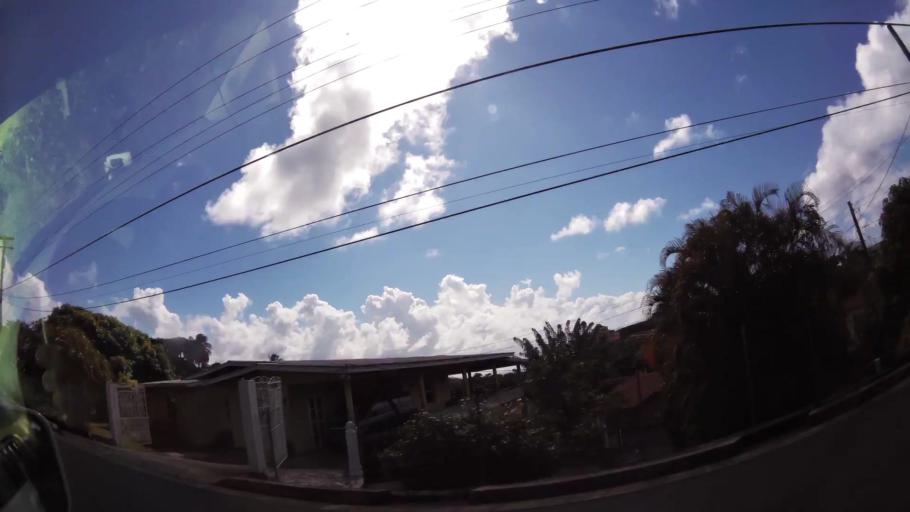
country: VC
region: Saint George
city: Kingstown
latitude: 13.1312
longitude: -61.1874
